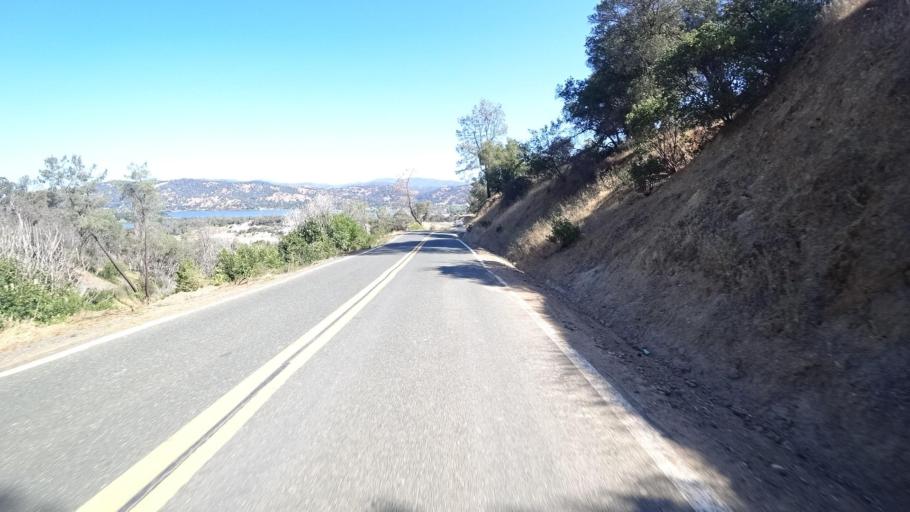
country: US
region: California
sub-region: Lake County
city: Clearlake Oaks
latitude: 38.9977
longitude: -122.6614
